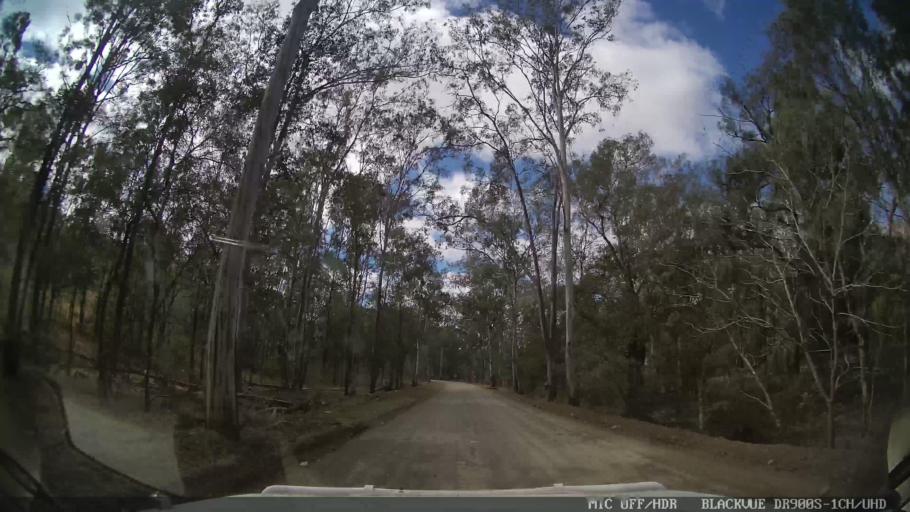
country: AU
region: Queensland
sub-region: Gladstone
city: Toolooa
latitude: -24.5511
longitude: 151.3396
